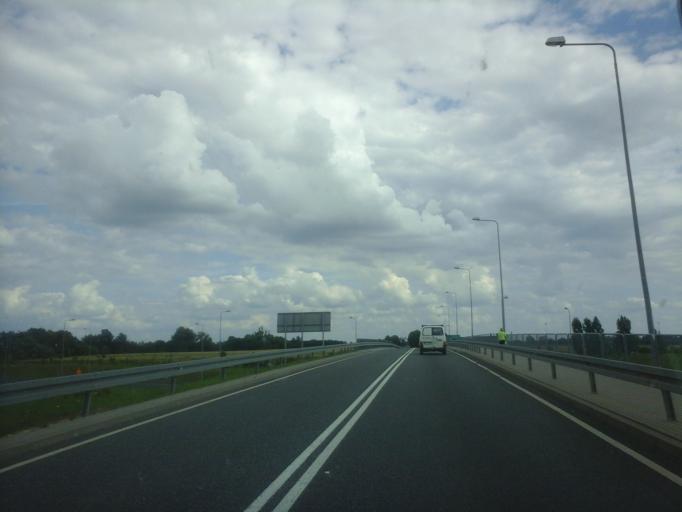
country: PL
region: West Pomeranian Voivodeship
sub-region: Powiat stargardzki
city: Stargard Szczecinski
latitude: 53.3153
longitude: 15.0934
